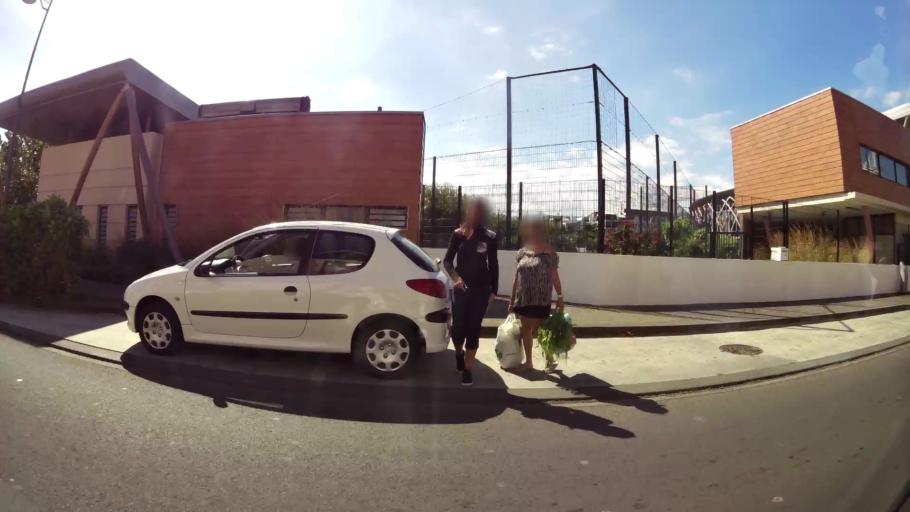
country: RE
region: Reunion
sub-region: Reunion
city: Saint-Pierre
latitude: -21.3388
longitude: 55.4625
